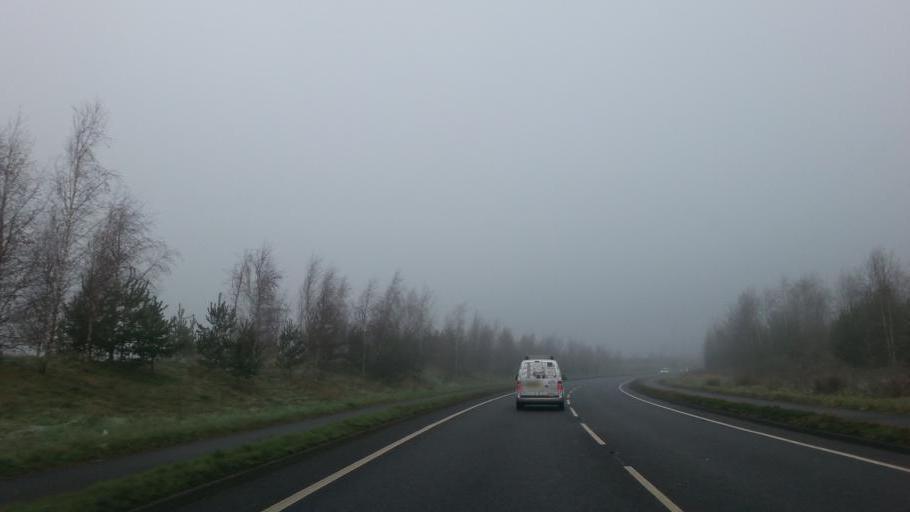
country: GB
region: England
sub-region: Cheshire East
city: Alderley Edge
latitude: 53.2905
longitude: -2.2551
